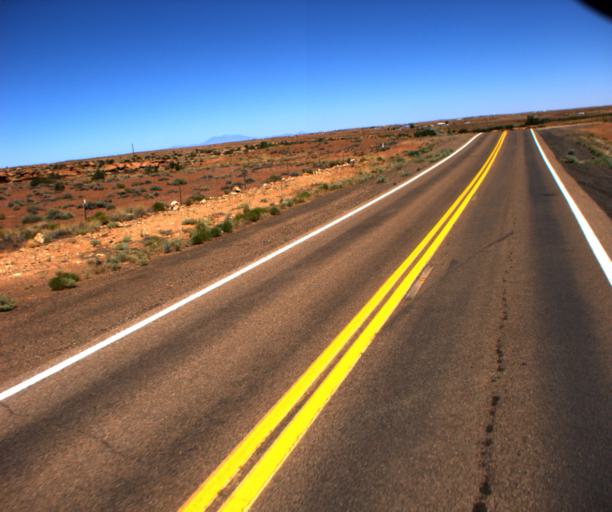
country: US
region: Arizona
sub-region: Navajo County
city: Winslow
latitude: 34.9722
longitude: -110.6490
